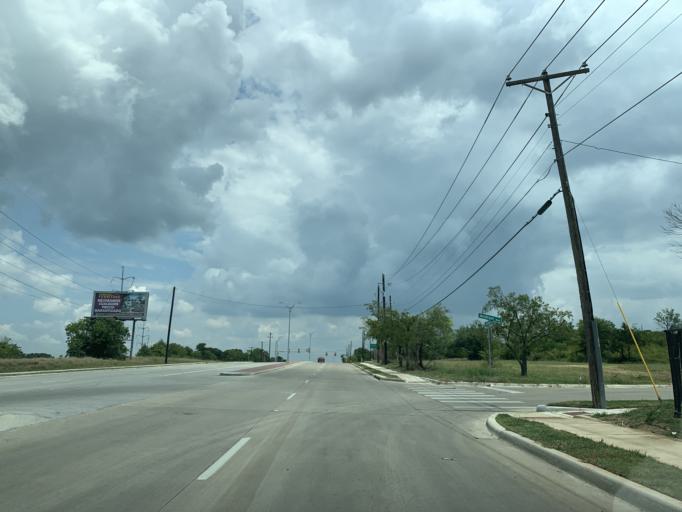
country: US
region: Texas
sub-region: Tarrant County
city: Forest Hill
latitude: 32.7305
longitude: -97.2396
